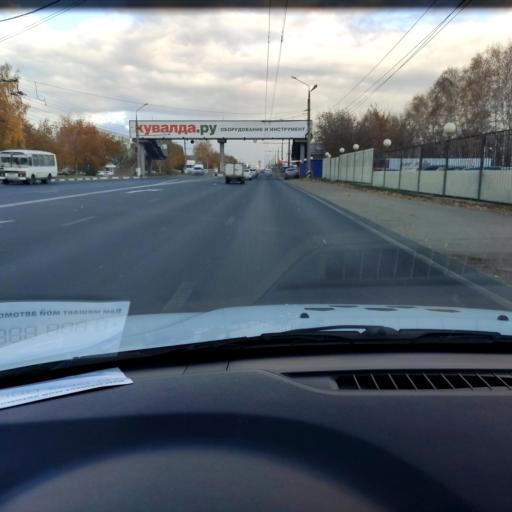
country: RU
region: Samara
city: Tol'yatti
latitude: 53.5518
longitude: 49.3051
